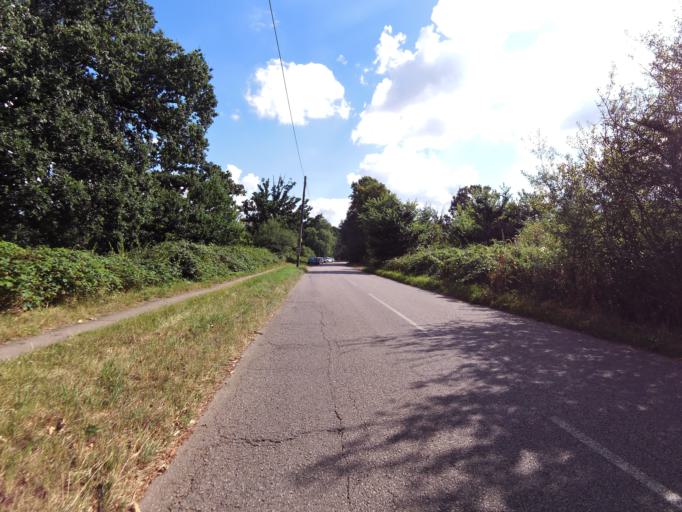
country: GB
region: England
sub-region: Greater London
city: High Barnet
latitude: 51.6612
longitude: -0.2291
